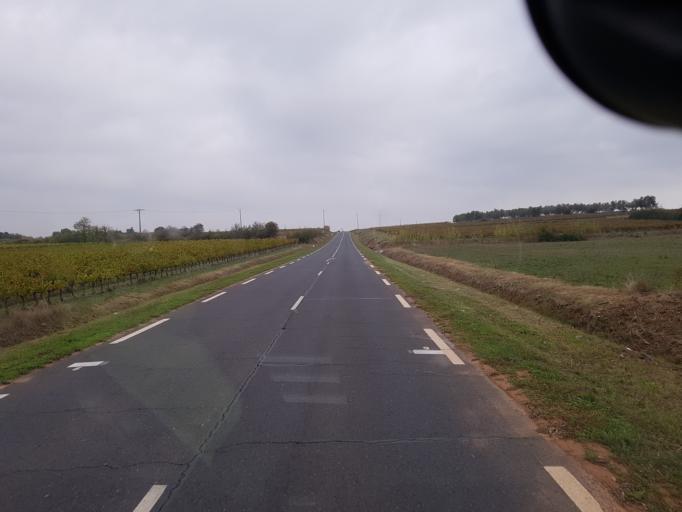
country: FR
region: Languedoc-Roussillon
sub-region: Departement de l'Herault
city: Marseillan
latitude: 43.3697
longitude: 3.5321
